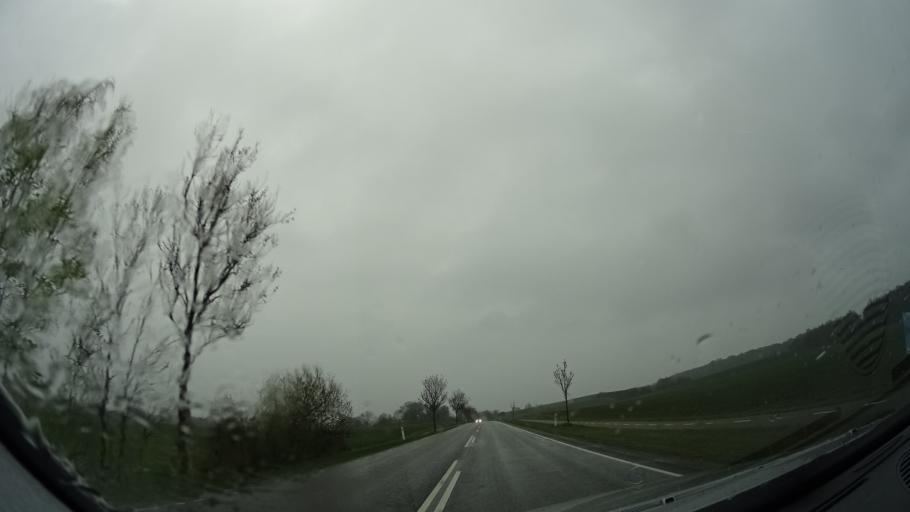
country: DK
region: Zealand
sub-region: Lejre Kommune
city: Ejby
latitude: 55.6746
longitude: 11.8333
